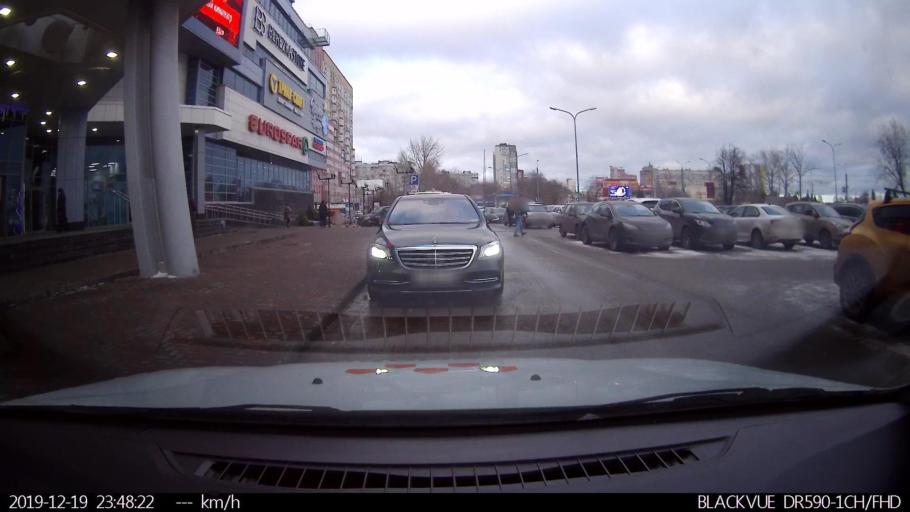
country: RU
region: Jaroslavl
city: Breytovo
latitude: 58.3823
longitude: 37.8772
